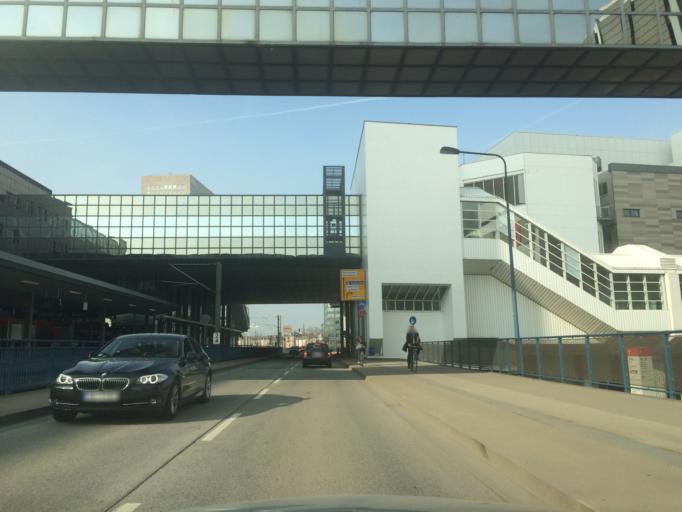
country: DE
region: Hesse
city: Niederrad
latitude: 50.1113
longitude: 8.6437
